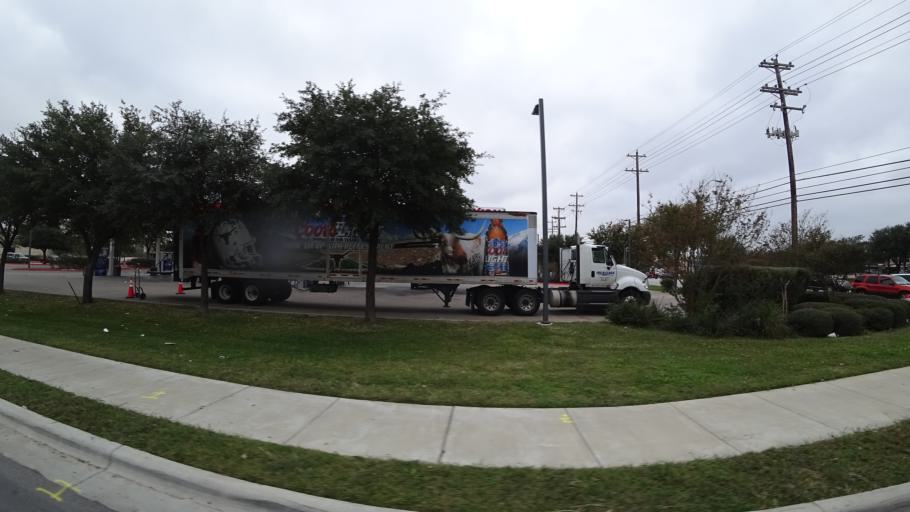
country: US
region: Texas
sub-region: Williamson County
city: Cedar Park
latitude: 30.4814
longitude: -97.8323
